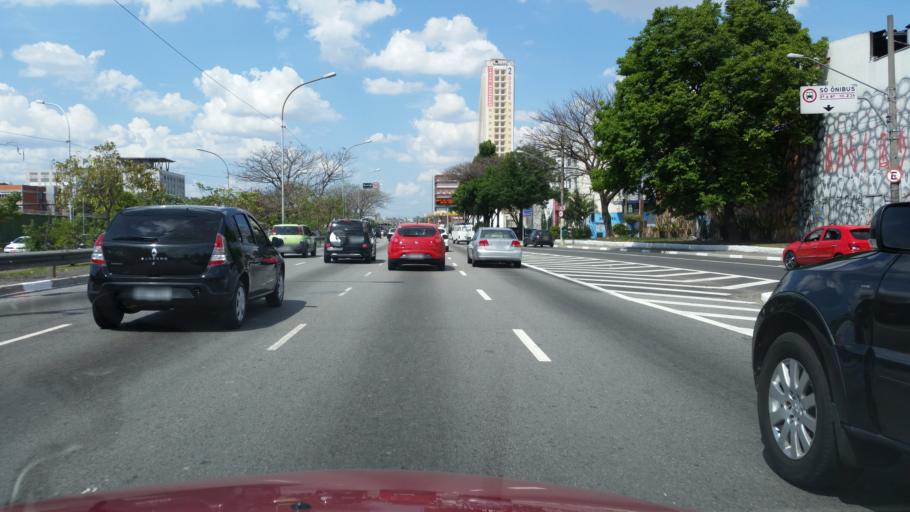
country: BR
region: Sao Paulo
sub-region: Sao Paulo
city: Sao Paulo
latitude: -23.5380
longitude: -46.5627
